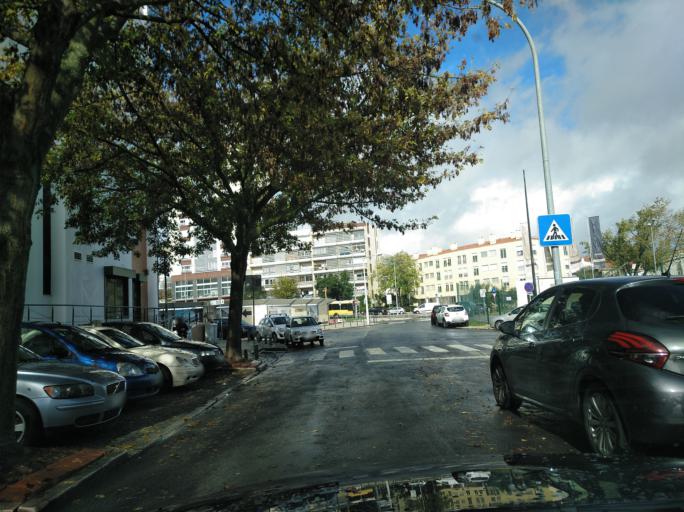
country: PT
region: Lisbon
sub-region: Loures
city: Moscavide
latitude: 38.7671
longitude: -9.1066
